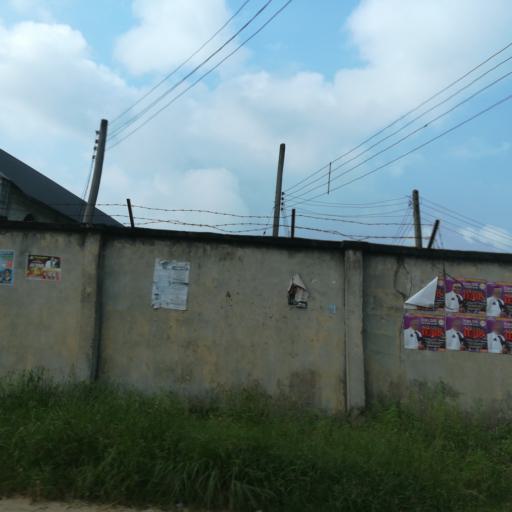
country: NG
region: Rivers
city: Okrika
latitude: 4.7787
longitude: 7.1556
